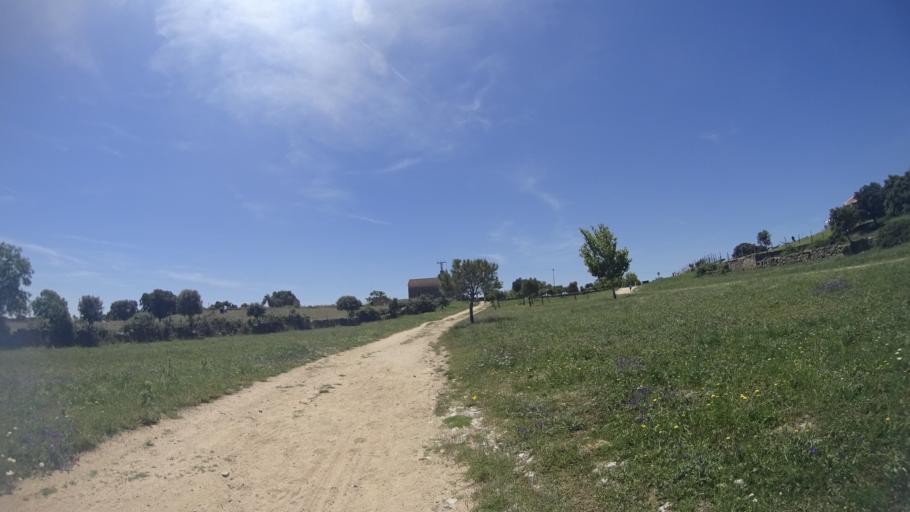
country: ES
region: Madrid
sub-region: Provincia de Madrid
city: Navalquejigo
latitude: 40.6124
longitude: -4.0362
